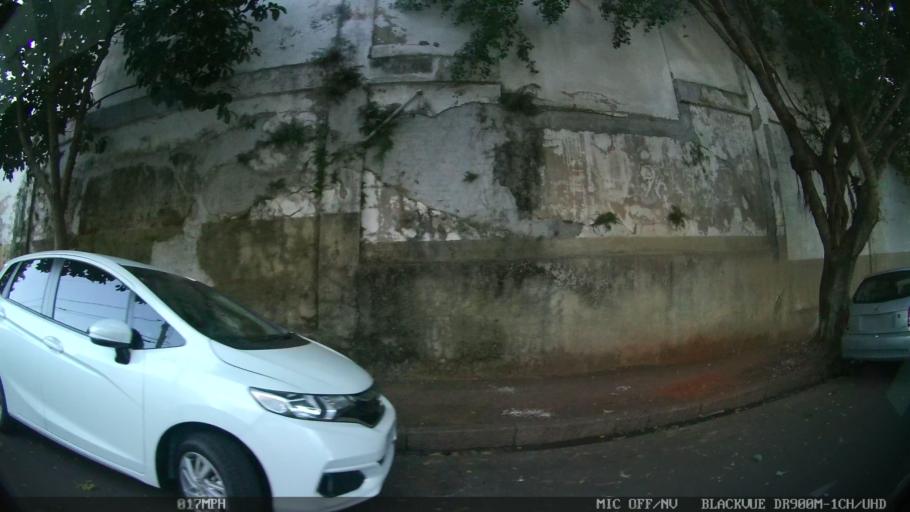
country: BR
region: Sao Paulo
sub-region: Santa Barbara D'Oeste
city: Santa Barbara d'Oeste
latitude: -22.7520
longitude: -47.4107
